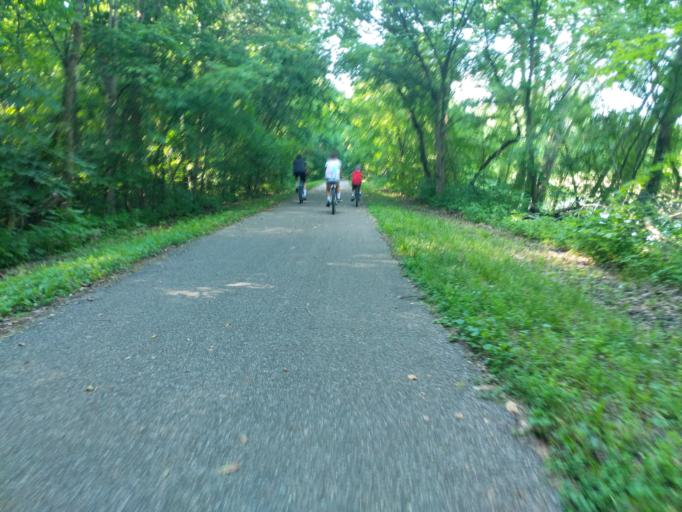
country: US
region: Ohio
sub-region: Athens County
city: Nelsonville
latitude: 39.4222
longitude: -82.1956
